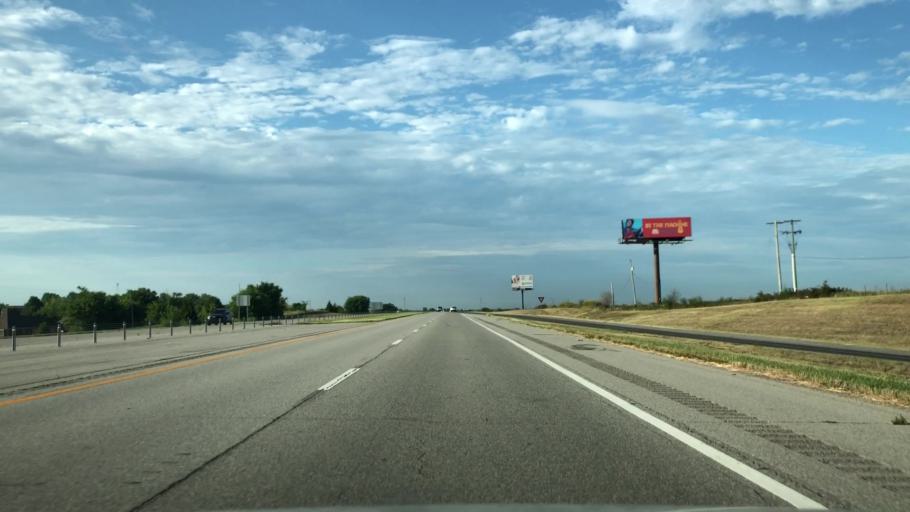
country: US
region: Oklahoma
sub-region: Osage County
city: Skiatook
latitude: 36.3638
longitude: -95.9208
